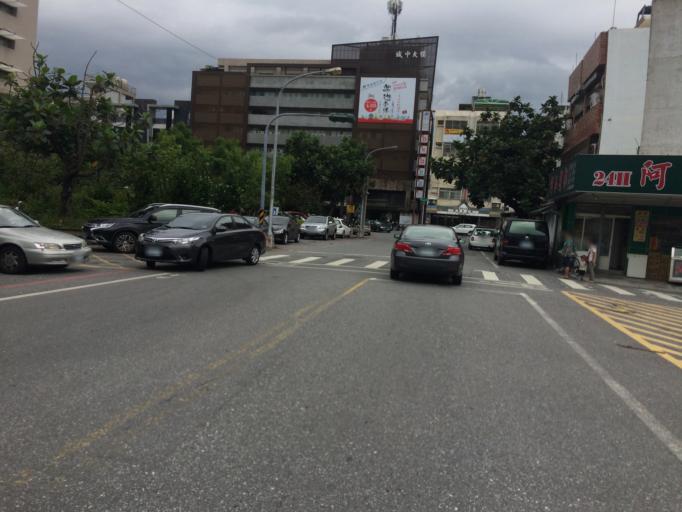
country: TW
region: Taiwan
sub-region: Hualien
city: Hualian
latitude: 23.9844
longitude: 121.6069
